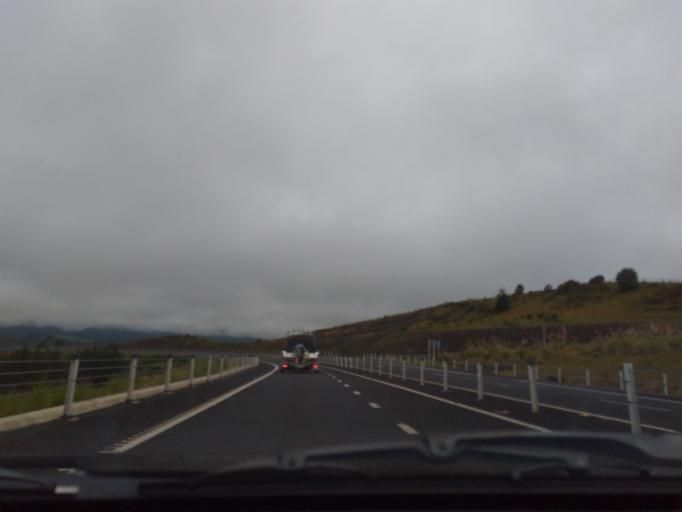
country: NZ
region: Northland
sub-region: Whangarei
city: Ruakaka
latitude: -36.0548
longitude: 174.4252
